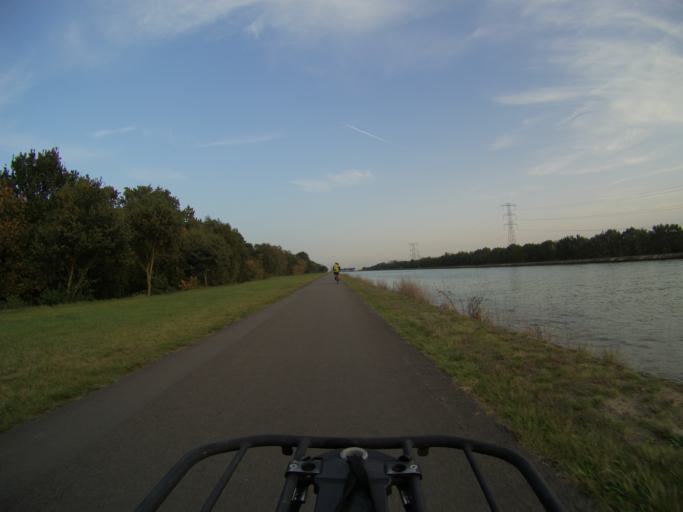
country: BE
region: Flanders
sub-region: Provincie Antwerpen
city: Nijlen
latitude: 51.1893
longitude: 4.6770
